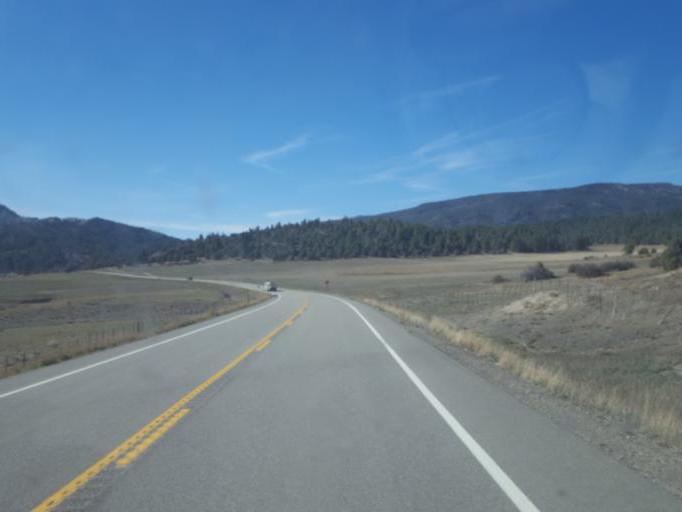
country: US
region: Colorado
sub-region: Archuleta County
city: Pagosa Springs
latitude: 37.2294
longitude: -107.1969
